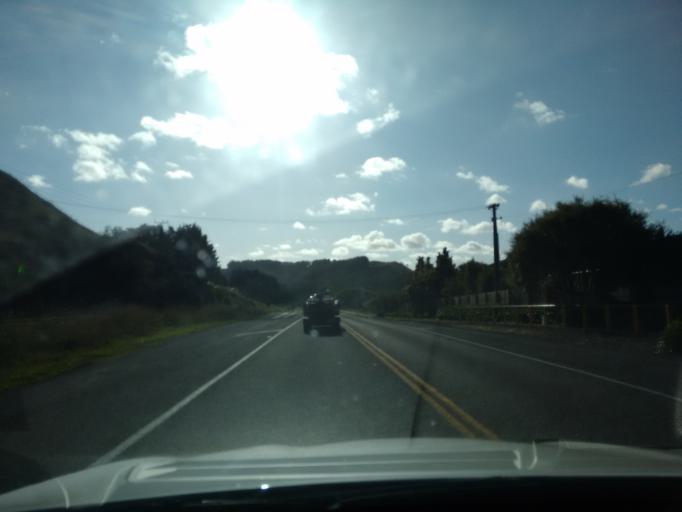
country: NZ
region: Manawatu-Wanganui
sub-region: Wanganui District
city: Wanganui
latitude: -39.8516
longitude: 174.9319
